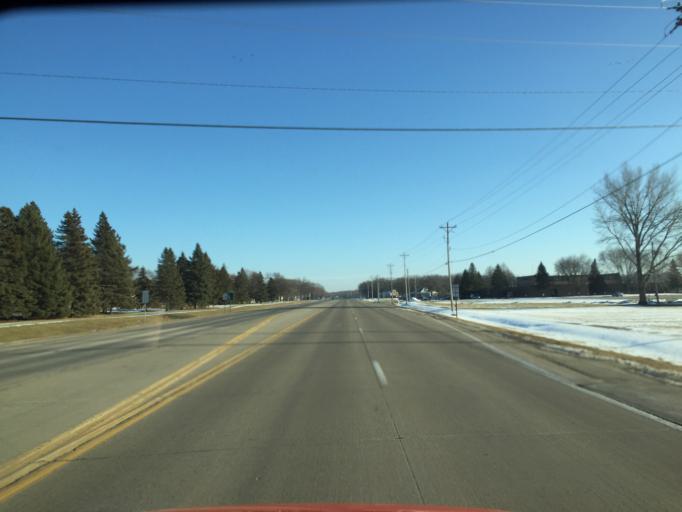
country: US
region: Minnesota
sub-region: Olmsted County
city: Rochester
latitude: 43.9987
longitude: -92.4323
